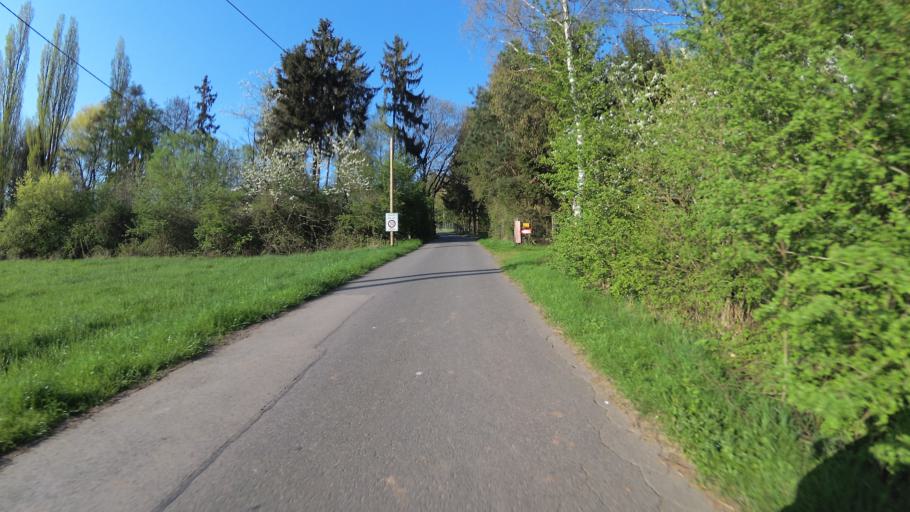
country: DE
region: Saarland
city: Schiffweiler
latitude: 49.3797
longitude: 7.0921
